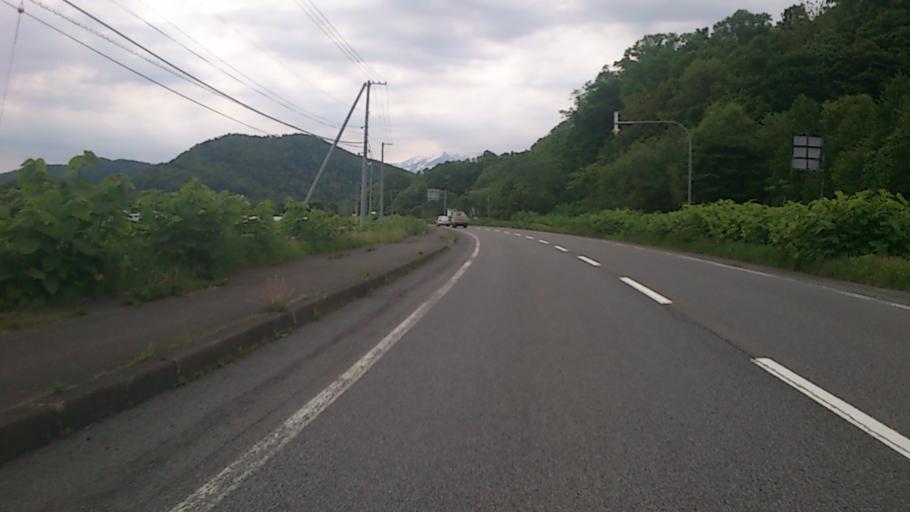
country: JP
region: Hokkaido
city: Kamikawa
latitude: 43.8471
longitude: 142.6964
